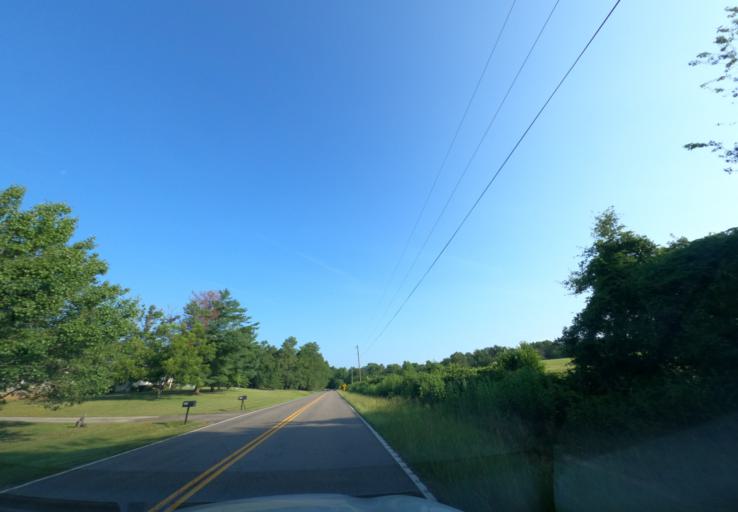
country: US
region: South Carolina
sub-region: Edgefield County
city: Murphys Estates
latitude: 33.6208
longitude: -81.9691
